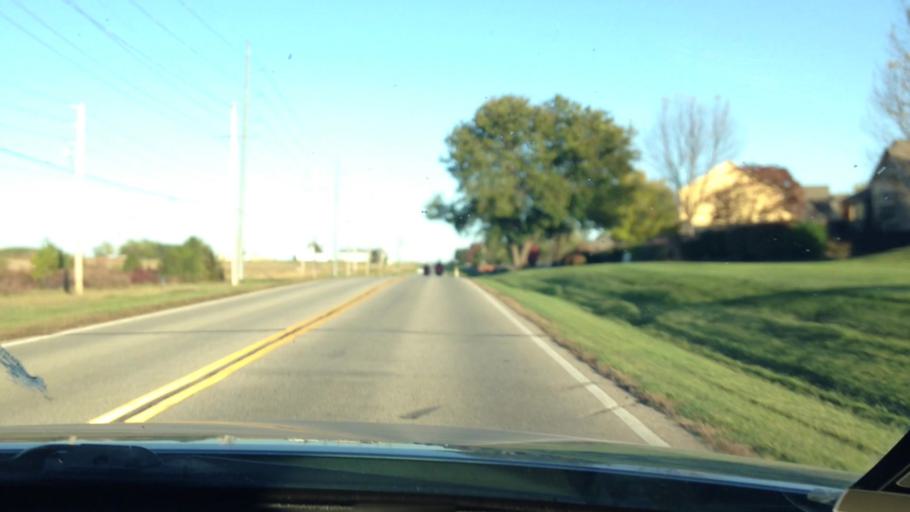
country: US
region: Kansas
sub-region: Johnson County
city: Gardner
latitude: 38.8255
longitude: -94.9163
